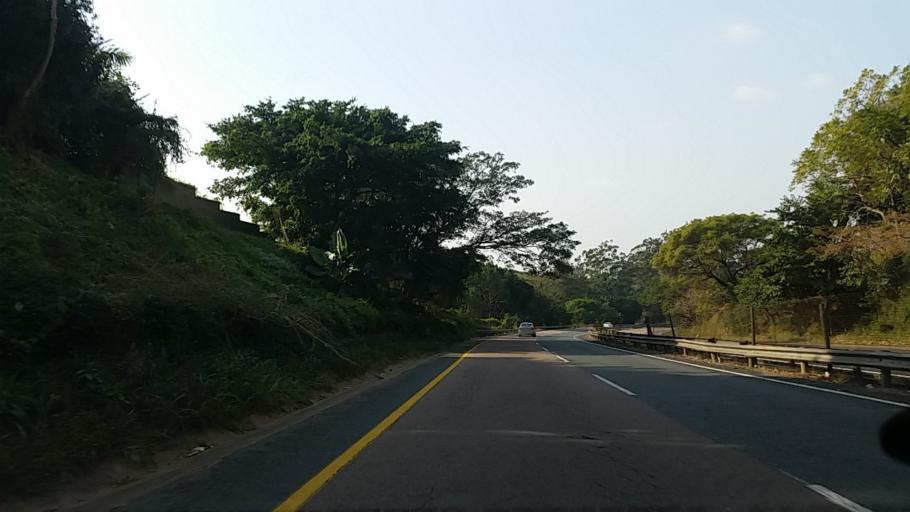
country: ZA
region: KwaZulu-Natal
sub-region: eThekwini Metropolitan Municipality
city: Berea
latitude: -29.8325
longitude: 30.9234
